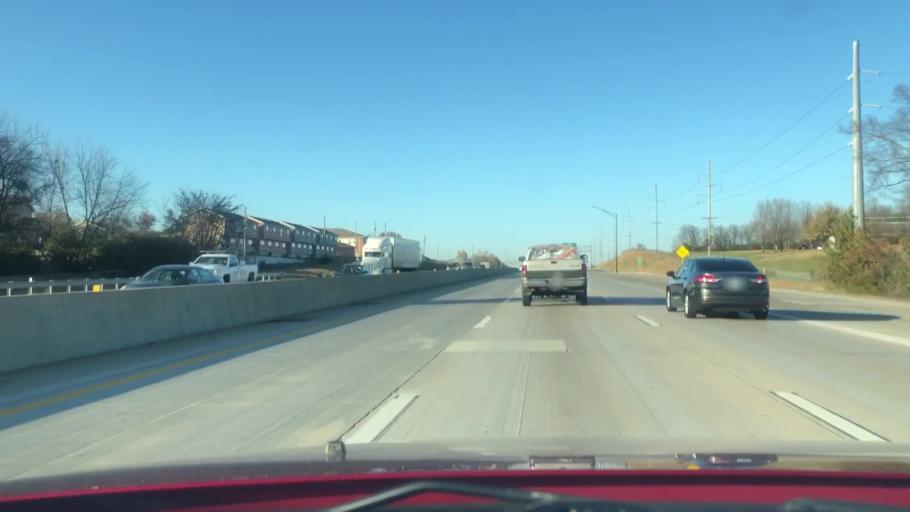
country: US
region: Missouri
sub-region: Greene County
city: Springfield
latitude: 37.1610
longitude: -93.2241
